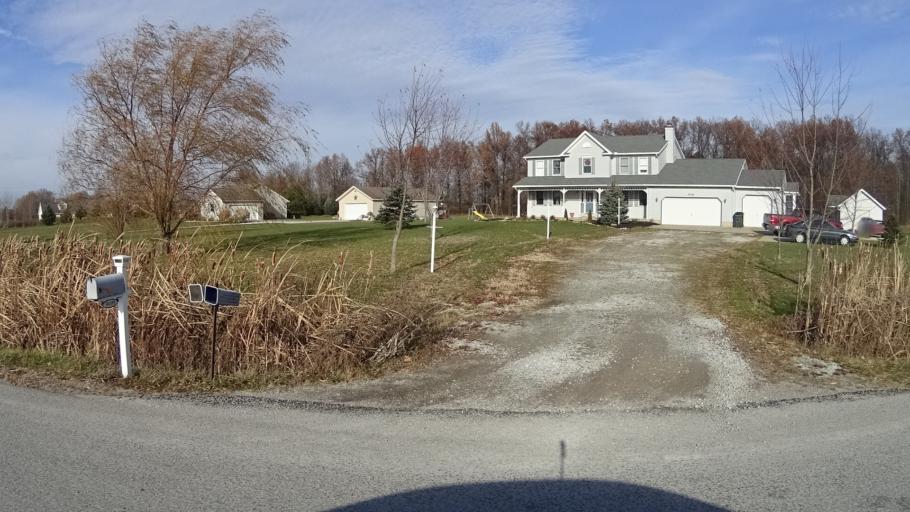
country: US
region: Ohio
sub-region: Lorain County
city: Grafton
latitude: 41.2286
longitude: -82.0397
